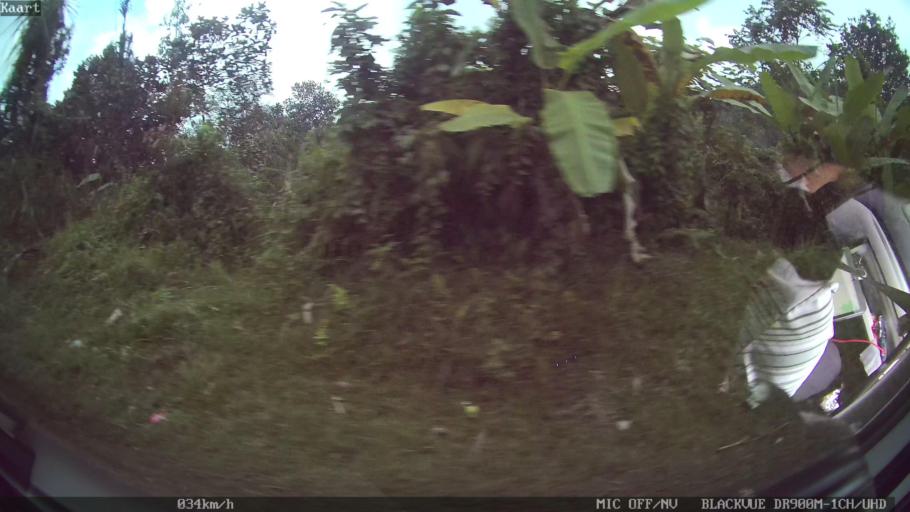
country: ID
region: Bali
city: Petang
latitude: -8.3650
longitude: 115.2228
